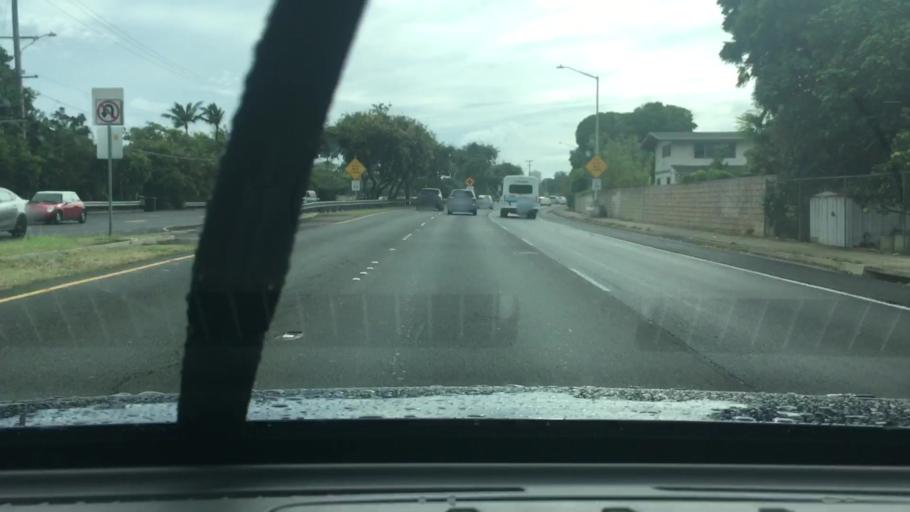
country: US
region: Hawaii
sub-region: Honolulu County
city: Waimanalo
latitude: 21.2761
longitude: -157.7650
